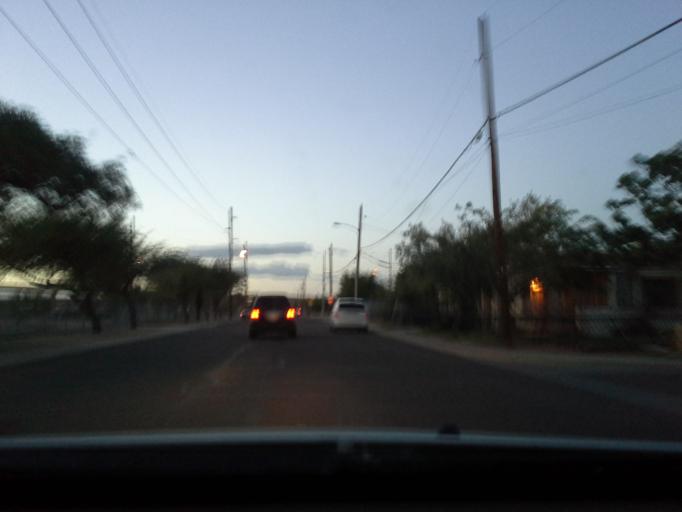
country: US
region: Arizona
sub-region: Maricopa County
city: Phoenix
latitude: 33.4576
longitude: -112.0357
